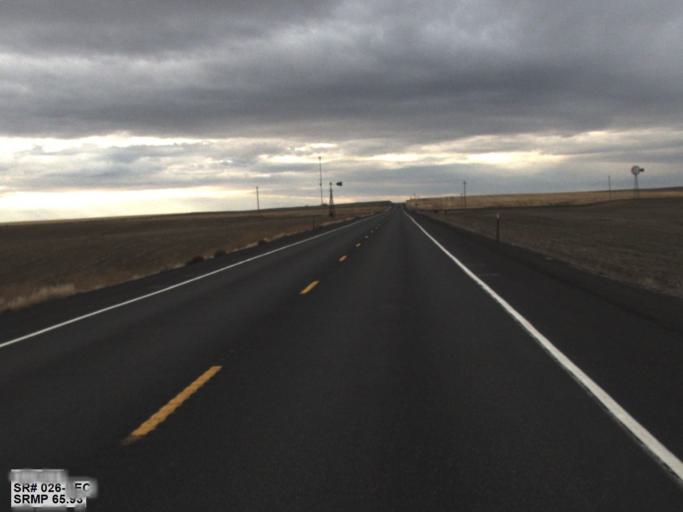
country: US
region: Washington
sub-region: Franklin County
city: Connell
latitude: 46.7944
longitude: -118.6455
